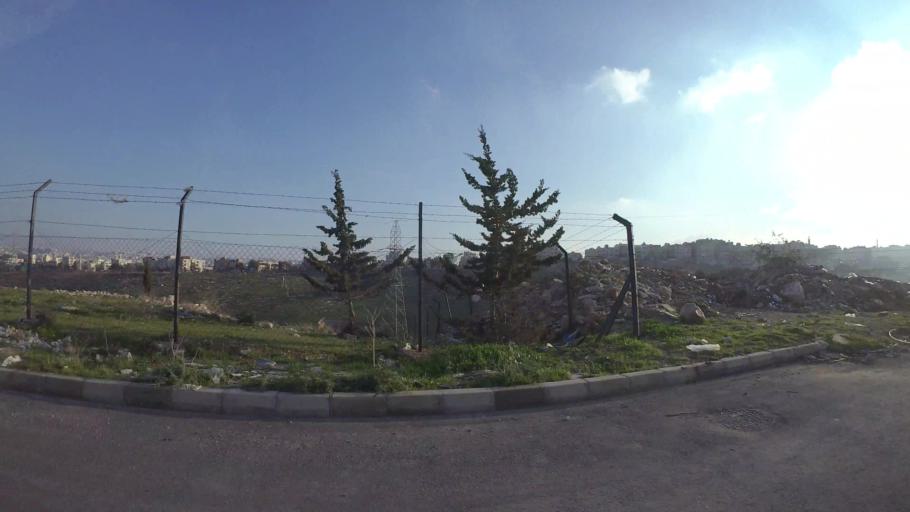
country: JO
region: Amman
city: Amman
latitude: 31.9831
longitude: 35.9616
